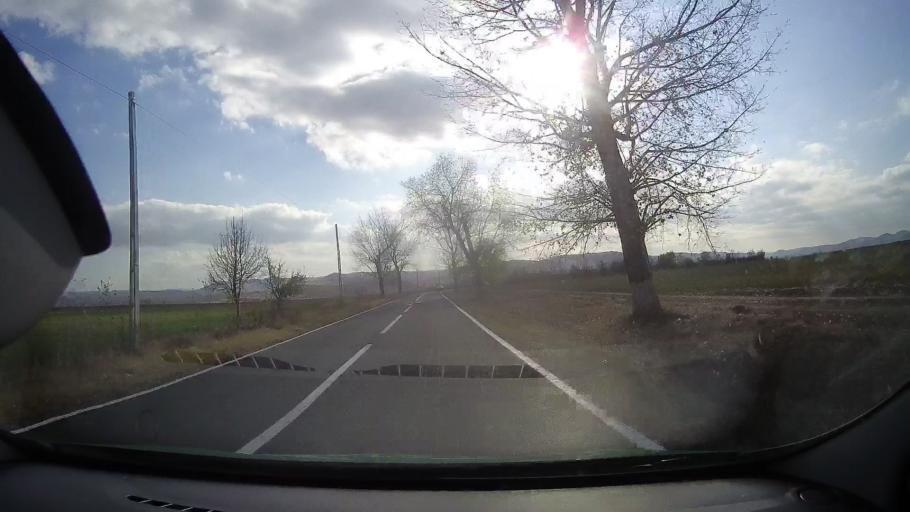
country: RO
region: Tulcea
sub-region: Comuna Nalbant
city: Nicolae Balcescu
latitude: 45.0048
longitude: 28.5973
